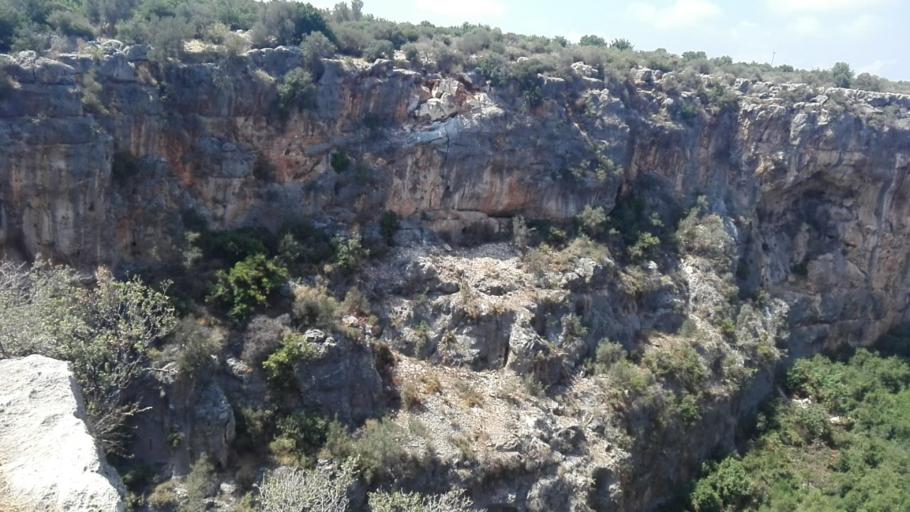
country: TR
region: Mersin
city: Silifke
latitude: 36.4517
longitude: 34.1053
